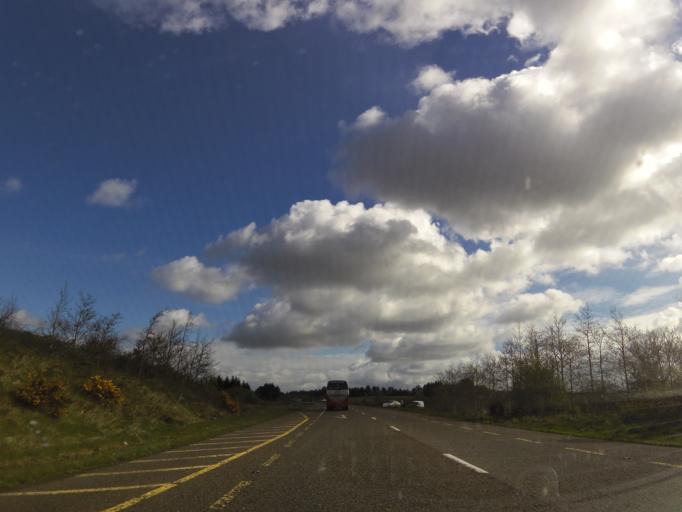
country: IE
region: Connaught
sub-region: Maigh Eo
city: Kiltamagh
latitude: 53.8089
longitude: -8.9047
